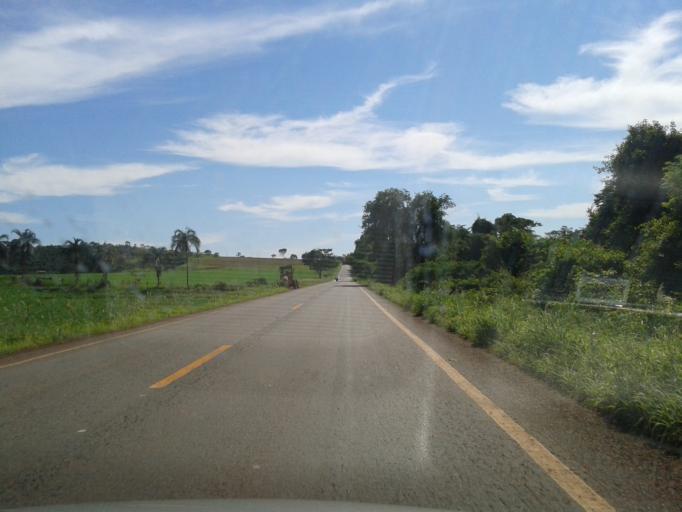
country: BR
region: Goias
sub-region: Piracanjuba
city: Piracanjuba
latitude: -17.2343
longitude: -48.7266
